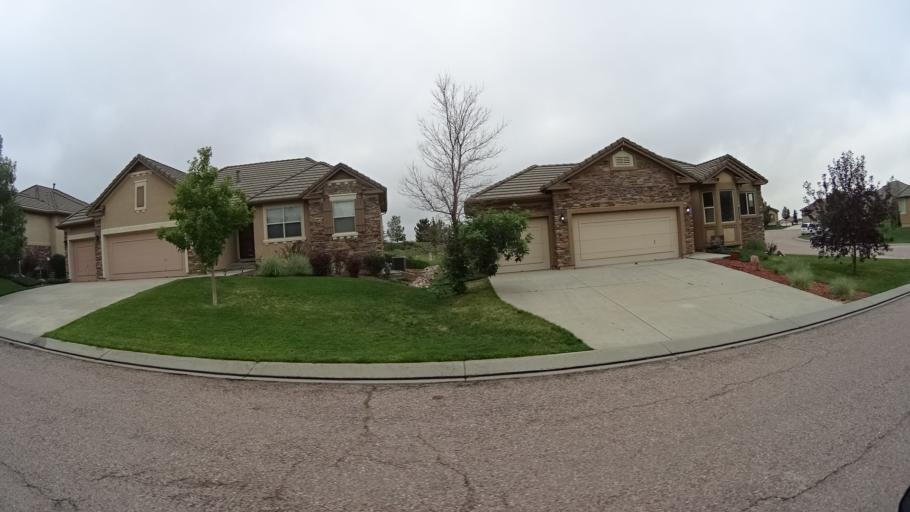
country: US
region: Colorado
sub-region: El Paso County
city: Gleneagle
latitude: 39.0319
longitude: -104.7782
